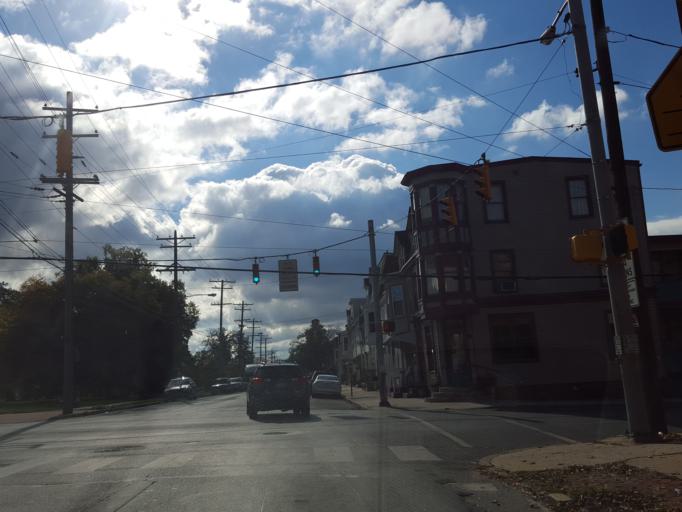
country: US
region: Pennsylvania
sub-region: York County
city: York
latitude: 39.9573
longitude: -76.7296
